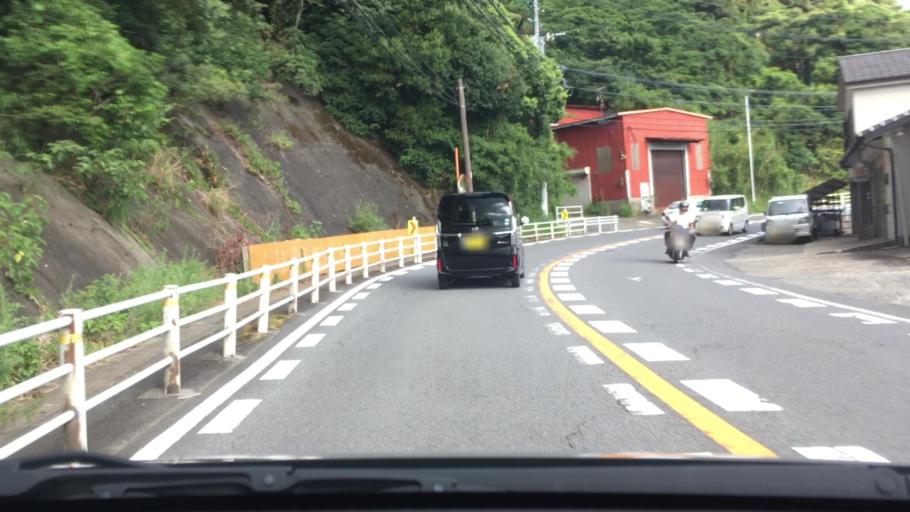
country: JP
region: Nagasaki
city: Togitsu
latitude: 32.8113
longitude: 129.8101
